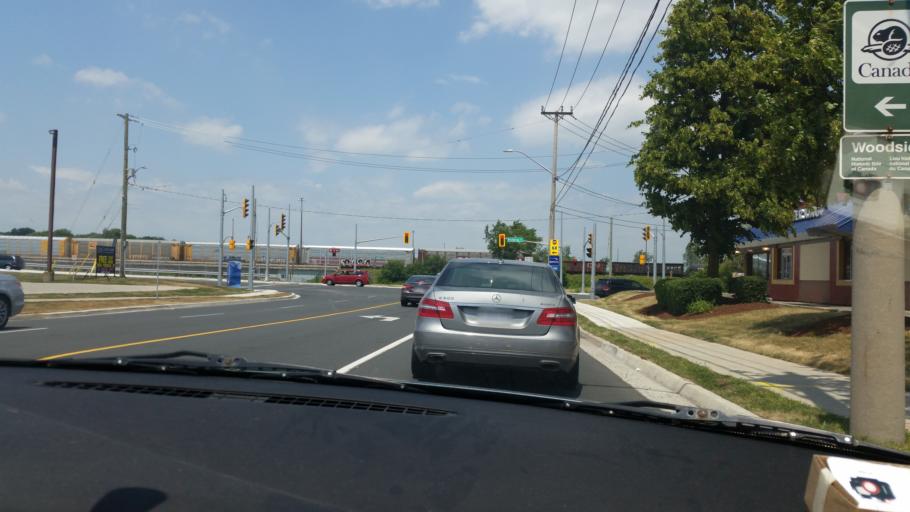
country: CA
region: Ontario
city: Waterloo
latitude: 43.4620
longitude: -80.4692
